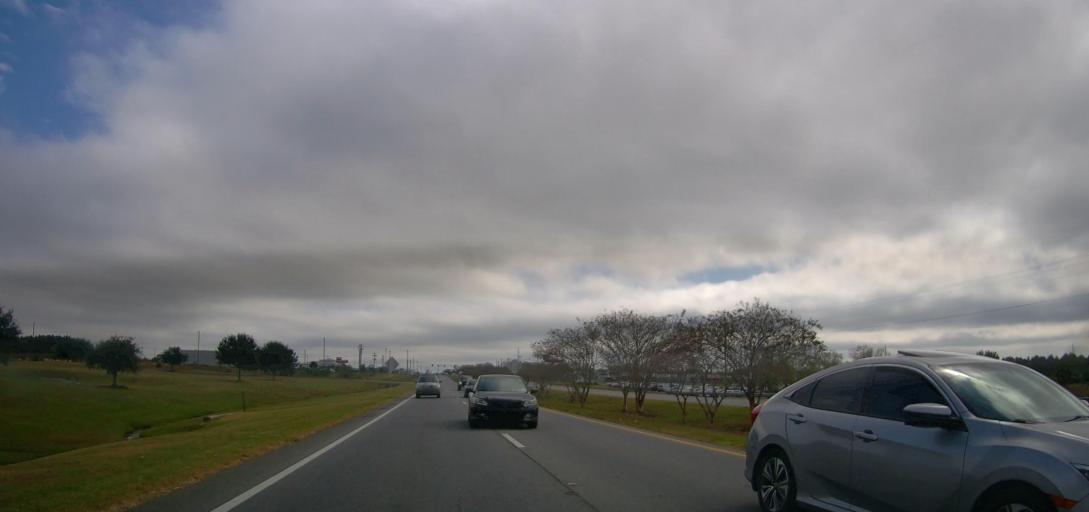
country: US
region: Georgia
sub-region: Colquitt County
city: Moultrie
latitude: 31.1970
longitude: -83.7682
